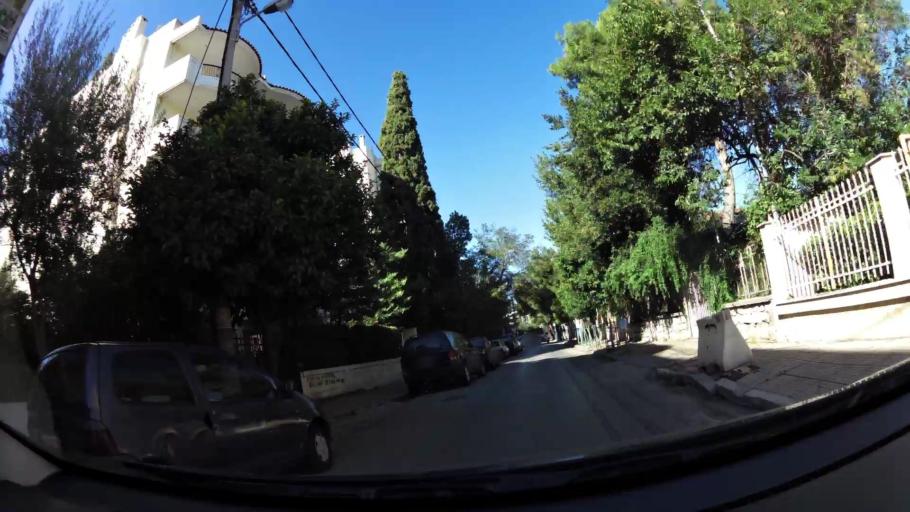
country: GR
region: Attica
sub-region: Nomarchia Athinas
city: Khalandrion
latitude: 38.0218
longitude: 23.8063
